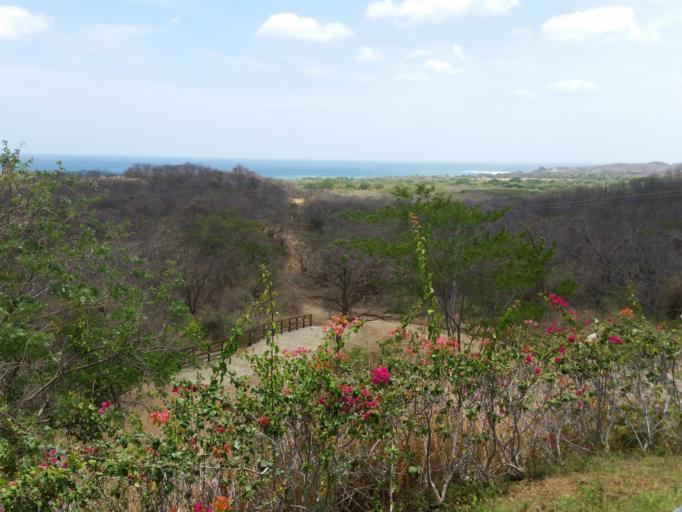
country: NI
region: Rivas
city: Tola
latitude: 11.4453
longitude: -86.0738
